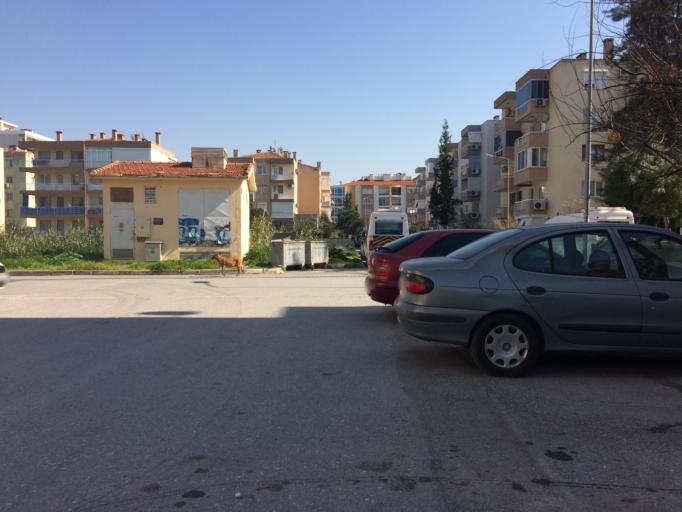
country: TR
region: Izmir
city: Karsiyaka
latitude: 38.4888
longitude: 27.0604
